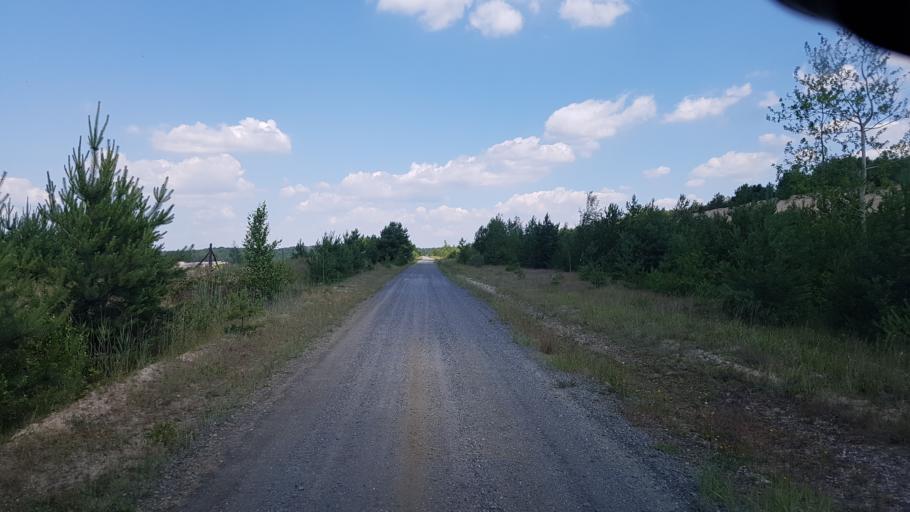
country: DE
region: Brandenburg
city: Sallgast
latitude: 51.5746
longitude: 13.8027
